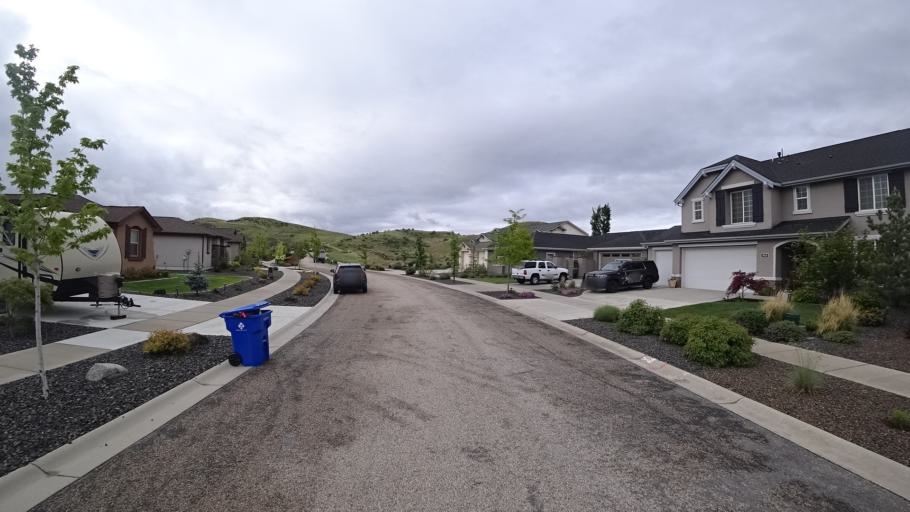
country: US
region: Idaho
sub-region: Ada County
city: Eagle
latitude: 43.7695
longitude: -116.2600
